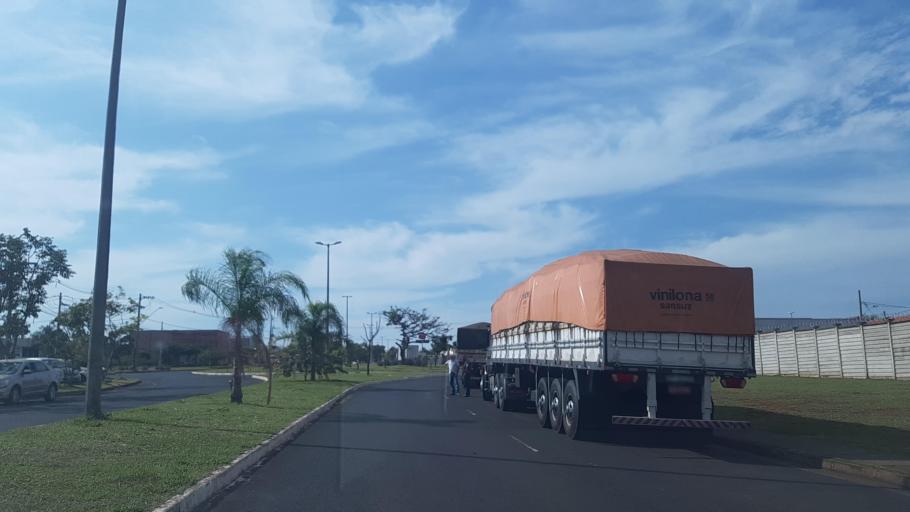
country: BR
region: Minas Gerais
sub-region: Uberlandia
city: Uberlandia
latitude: -18.8730
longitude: -48.2313
